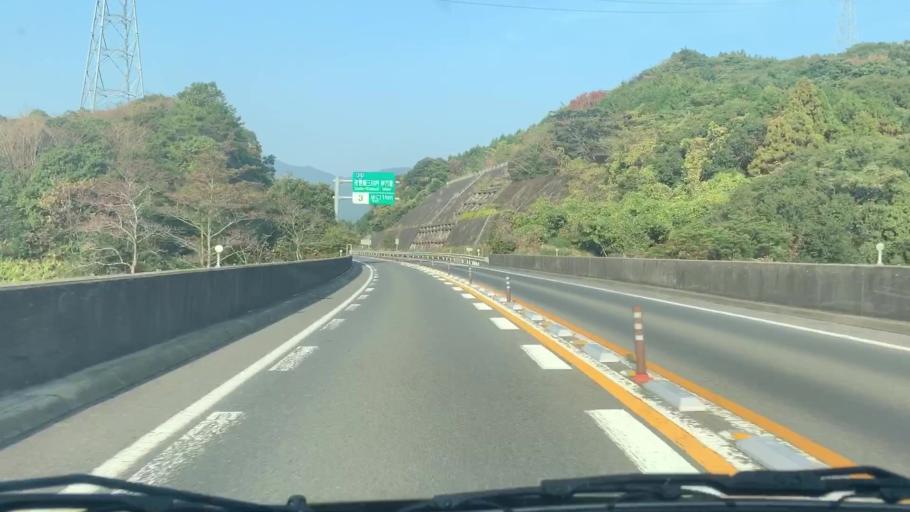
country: JP
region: Saga Prefecture
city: Imaricho-ko
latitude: 33.1653
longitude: 129.8609
